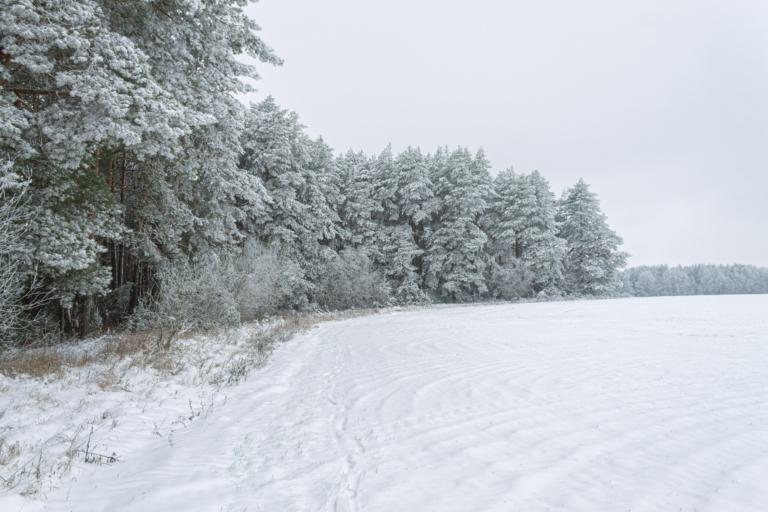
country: BY
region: Brest
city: Kamyanyets
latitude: 52.3774
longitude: 23.8448
